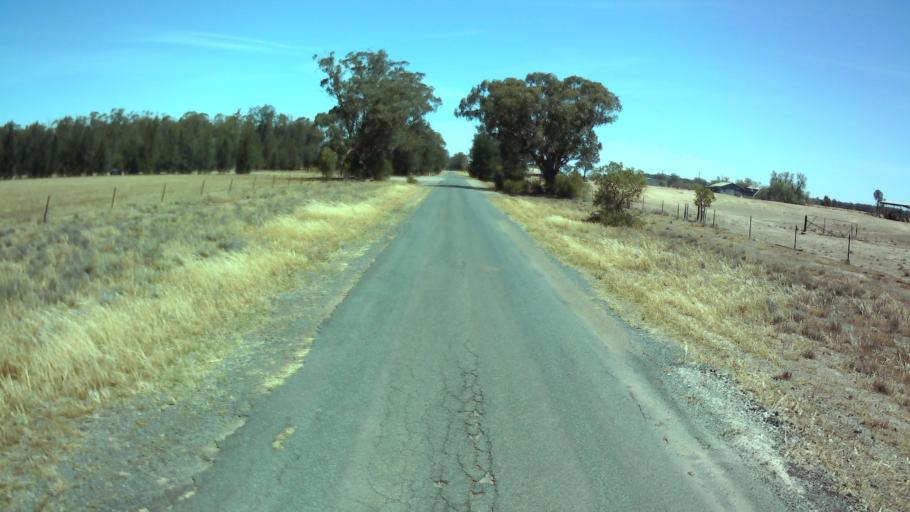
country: AU
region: New South Wales
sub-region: Weddin
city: Grenfell
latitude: -33.9022
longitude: 147.6861
